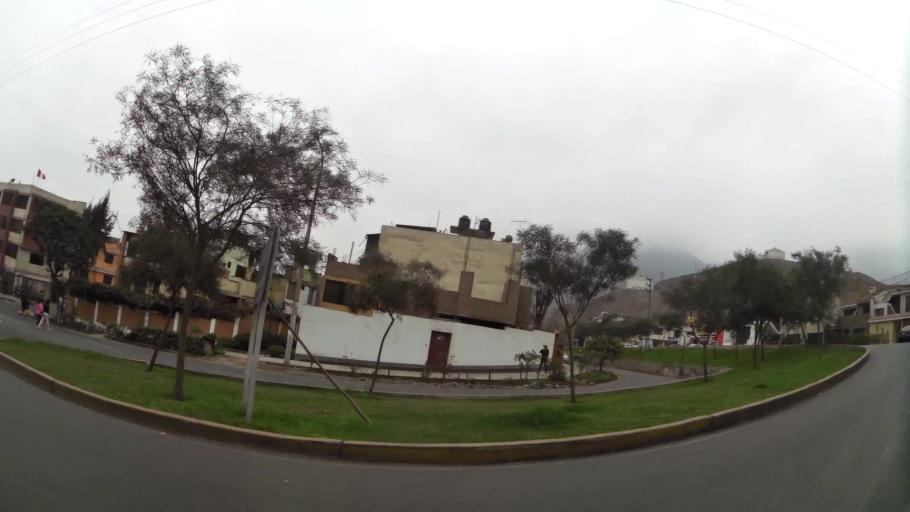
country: PE
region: Lima
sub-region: Lima
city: La Molina
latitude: -12.1161
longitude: -76.9394
